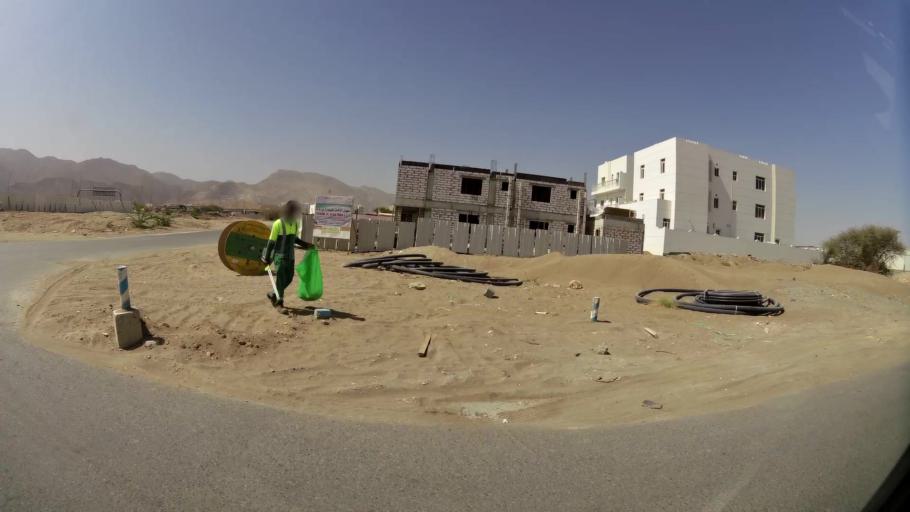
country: OM
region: Muhafazat Masqat
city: Bawshar
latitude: 23.5864
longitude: 58.4144
